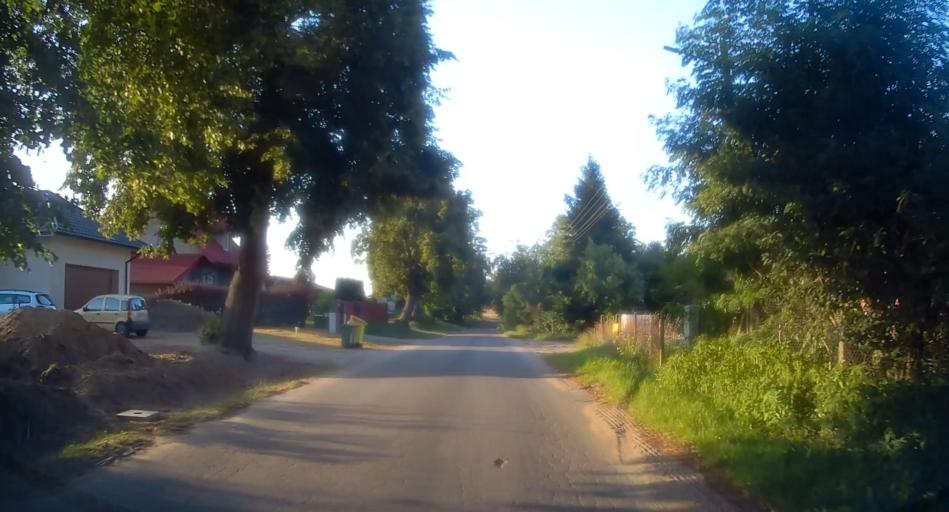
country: PL
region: Lodz Voivodeship
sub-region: Powiat skierniewicki
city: Kaweczyn Nowy
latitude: 51.8827
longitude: 20.2792
